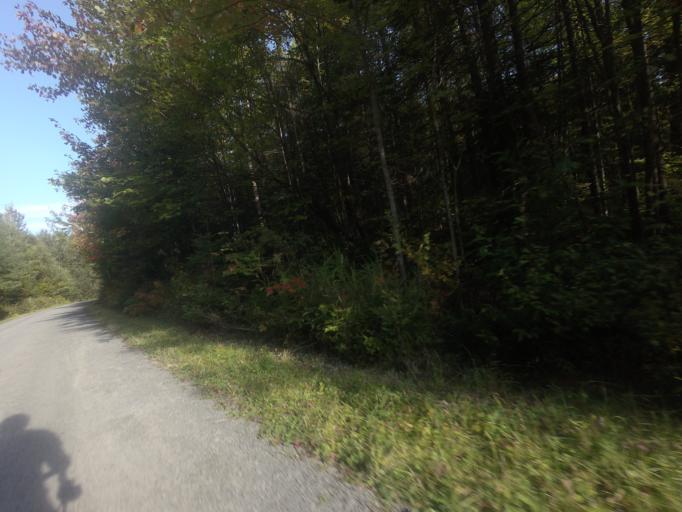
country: CA
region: Quebec
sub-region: Laurentides
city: Val-David
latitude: 46.0145
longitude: -74.1810
